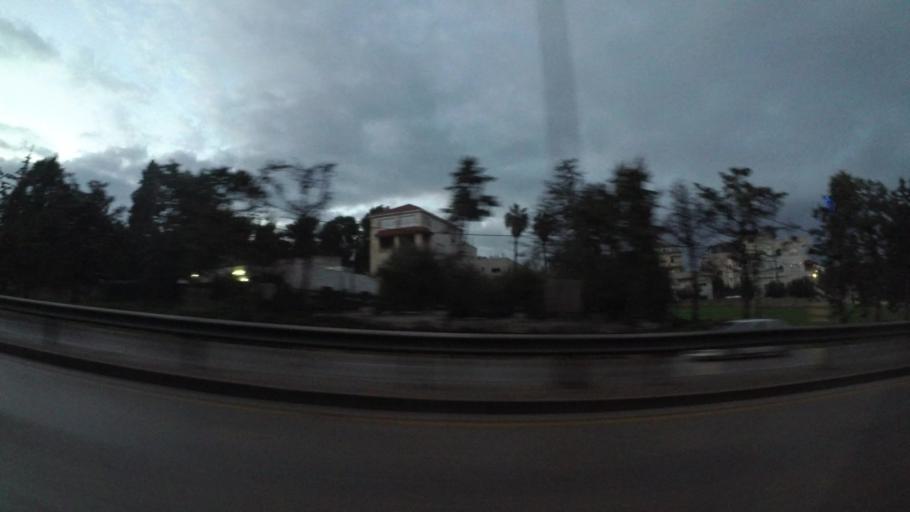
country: JO
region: Amman
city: Al Jubayhah
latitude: 32.0288
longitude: 35.8180
